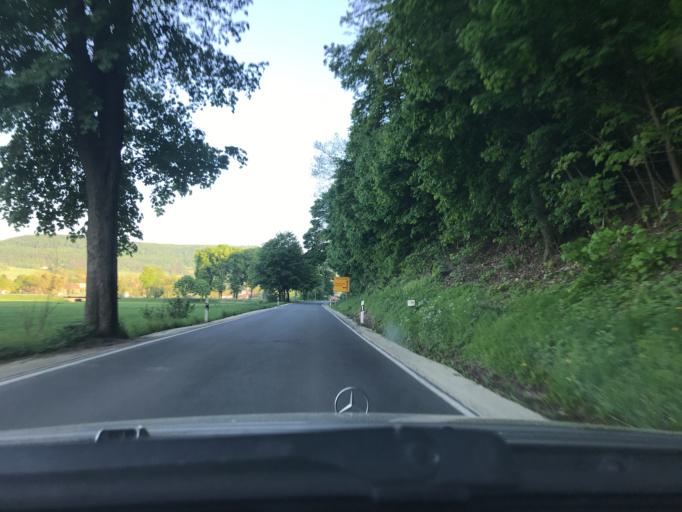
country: DE
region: Hesse
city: Wanfried
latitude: 51.1853
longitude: 10.1602
